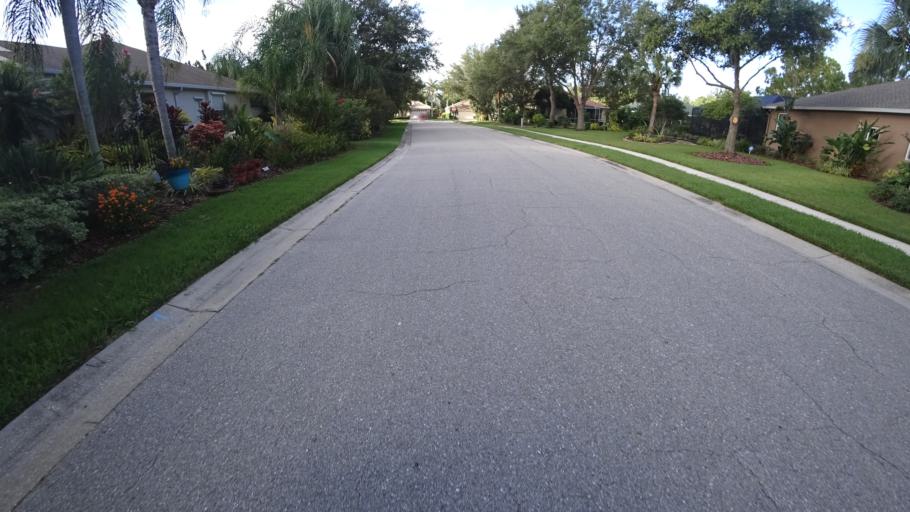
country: US
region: Florida
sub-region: Sarasota County
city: Desoto Lakes
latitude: 27.4228
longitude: -82.4940
